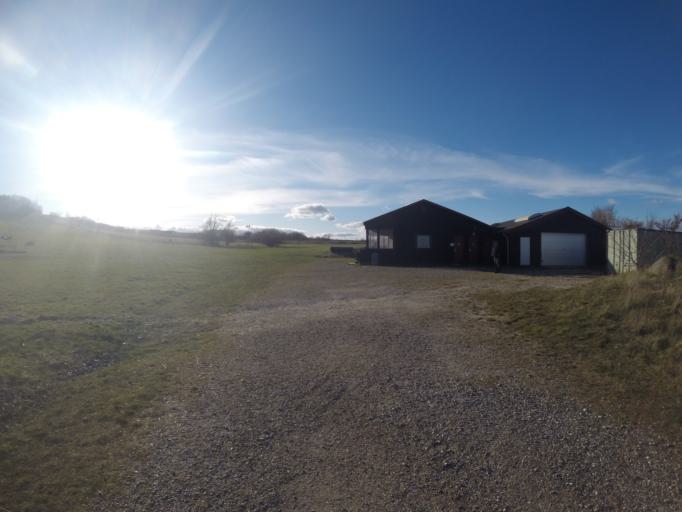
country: DK
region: Zealand
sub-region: Greve Kommune
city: Tune
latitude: 55.6278
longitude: 12.1756
